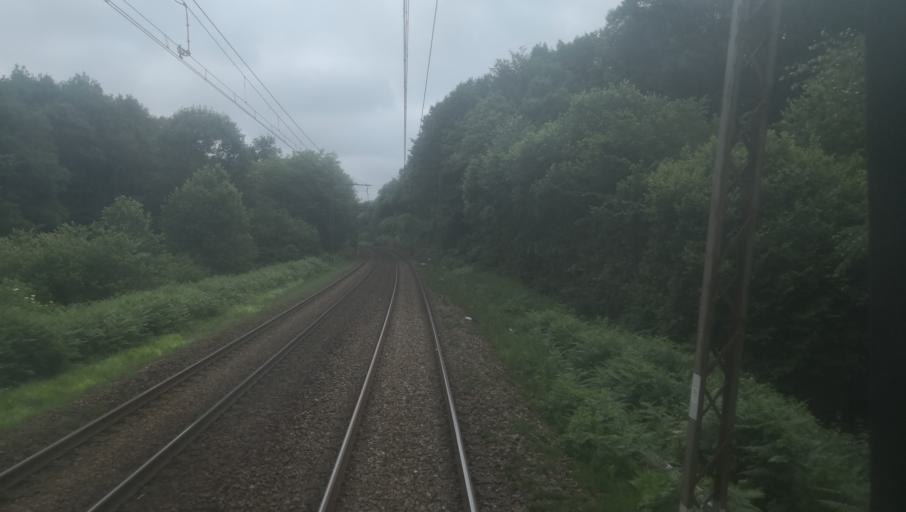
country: FR
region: Limousin
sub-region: Departement de la Haute-Vienne
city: Ambazac
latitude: 45.9664
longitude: 1.4533
